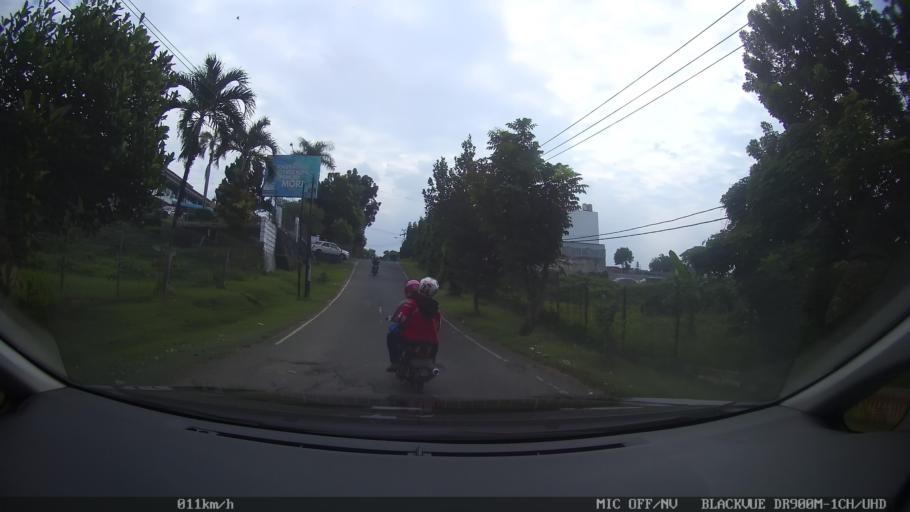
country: ID
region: Lampung
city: Bandarlampung
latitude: -5.4334
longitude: 105.2470
